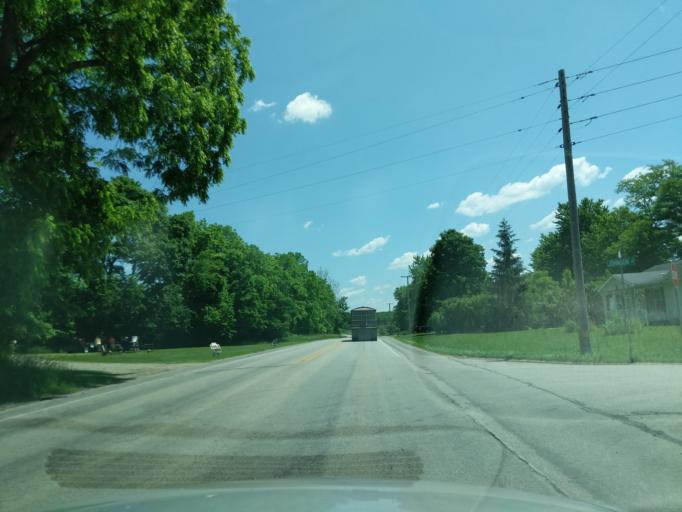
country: US
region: Indiana
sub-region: Noble County
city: Ligonier
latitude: 41.4747
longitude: -85.5826
